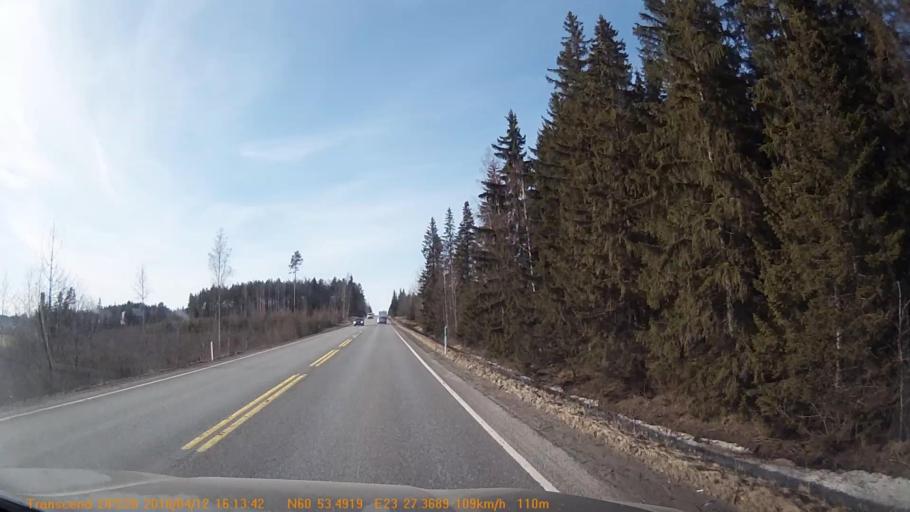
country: FI
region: Haeme
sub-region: Forssa
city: Jokioinen
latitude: 60.8916
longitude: 23.4560
